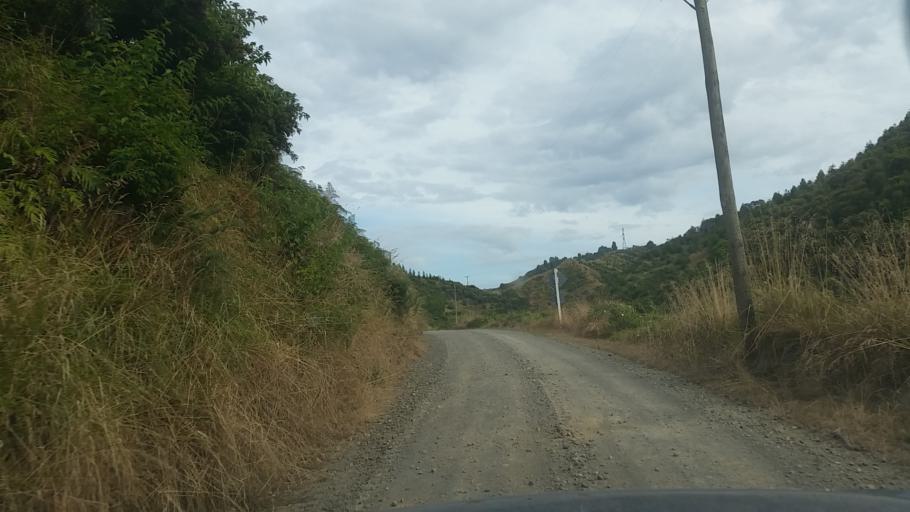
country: NZ
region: Taranaki
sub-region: New Plymouth District
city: Waitara
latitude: -39.1419
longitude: 174.7199
